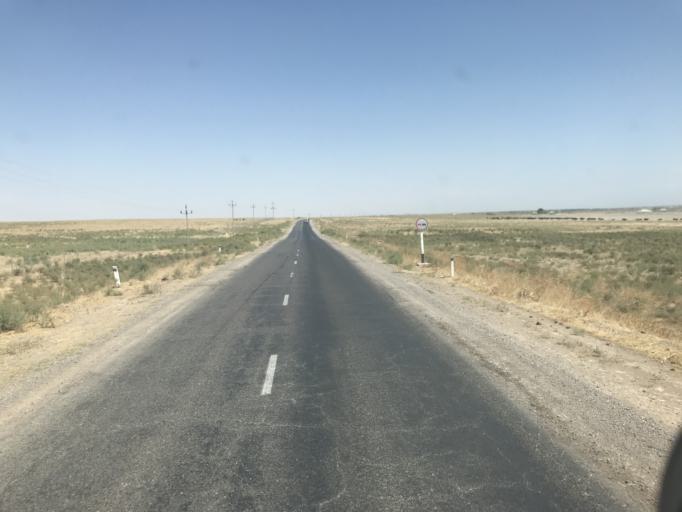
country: UZ
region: Toshkent
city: Amir Timur
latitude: 41.3575
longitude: 68.7205
